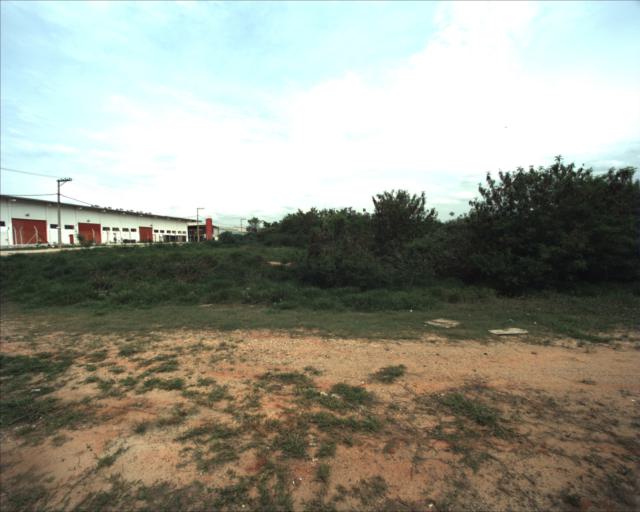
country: BR
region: Sao Paulo
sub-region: Sorocaba
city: Sorocaba
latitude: -23.4282
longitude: -47.4335
